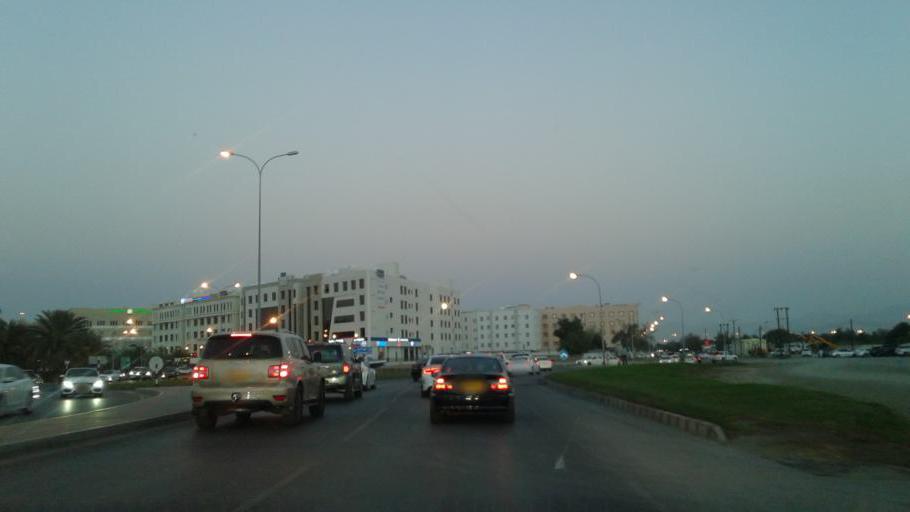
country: OM
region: Muhafazat Masqat
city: As Sib al Jadidah
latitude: 23.6107
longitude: 58.2407
